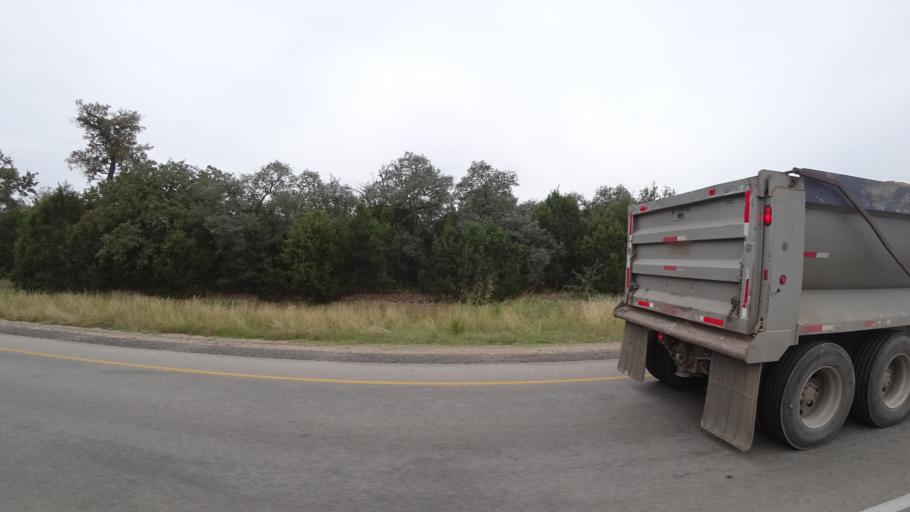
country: US
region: Texas
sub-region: Travis County
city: Shady Hollow
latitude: 30.1922
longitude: -97.9223
